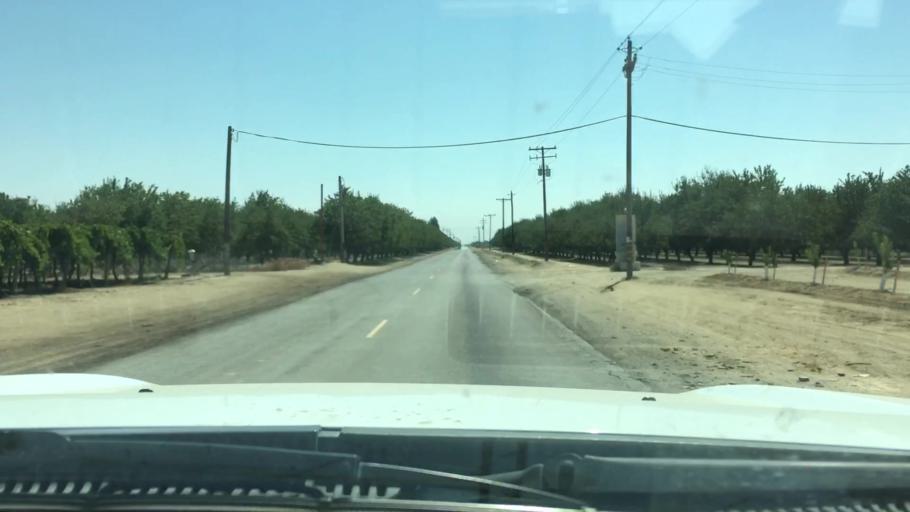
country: US
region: California
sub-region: Kern County
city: Shafter
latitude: 35.4894
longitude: -119.3140
